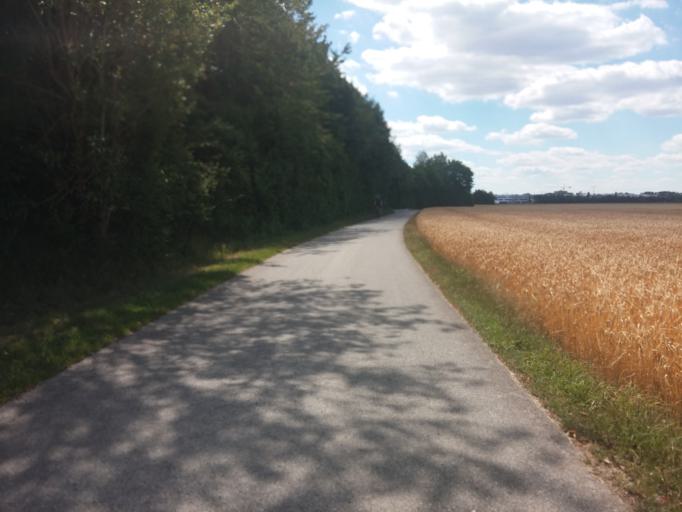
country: DE
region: Bavaria
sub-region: Upper Bavaria
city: Aschheim
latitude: 48.1477
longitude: 11.7041
